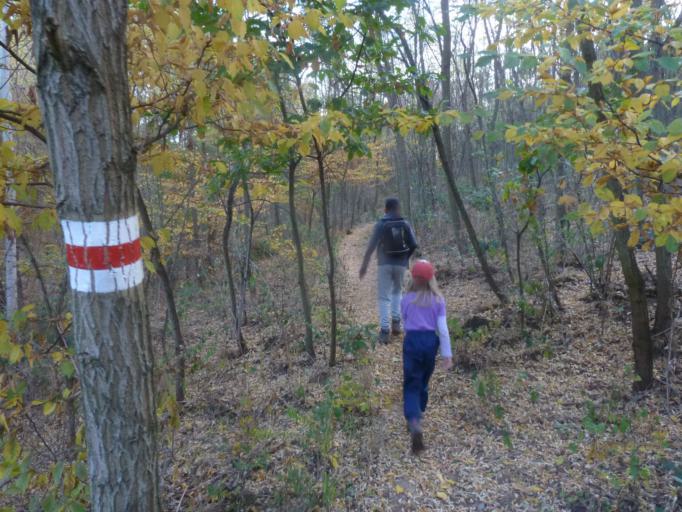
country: HU
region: Nograd
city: Salgotarjan
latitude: 48.1202
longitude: 19.8174
